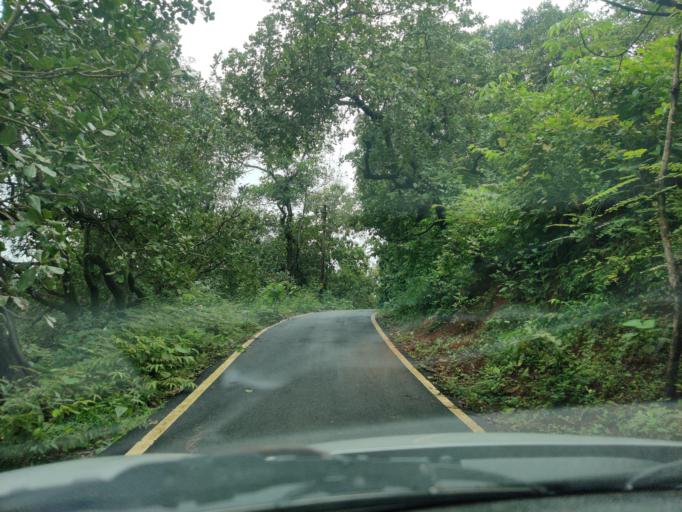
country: IN
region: Goa
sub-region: North Goa
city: Valpoy
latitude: 15.5287
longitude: 74.1424
